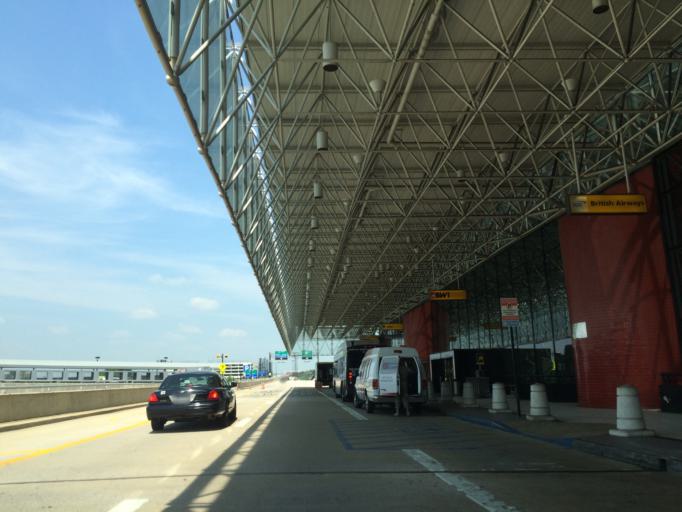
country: US
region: Maryland
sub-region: Anne Arundel County
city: Linthicum
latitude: 39.1818
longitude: -76.6691
